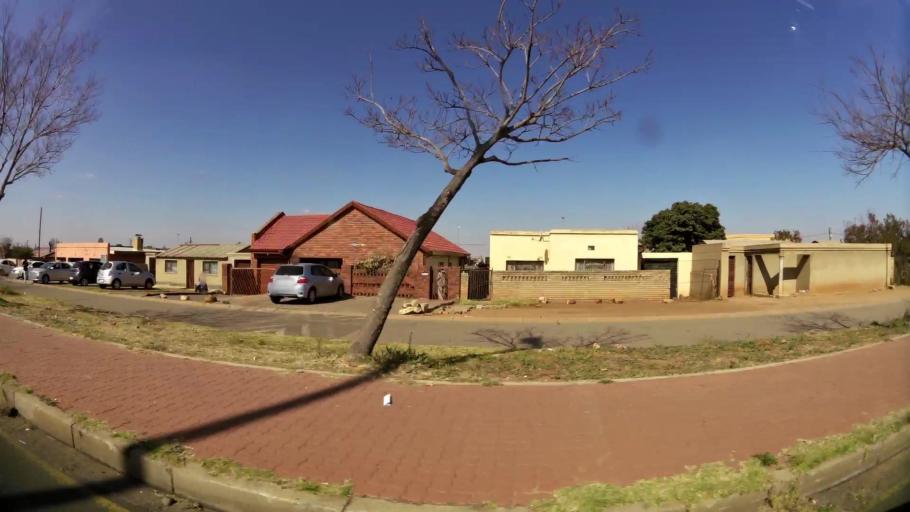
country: ZA
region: Gauteng
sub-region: City of Johannesburg Metropolitan Municipality
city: Soweto
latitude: -26.2777
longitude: 27.8656
